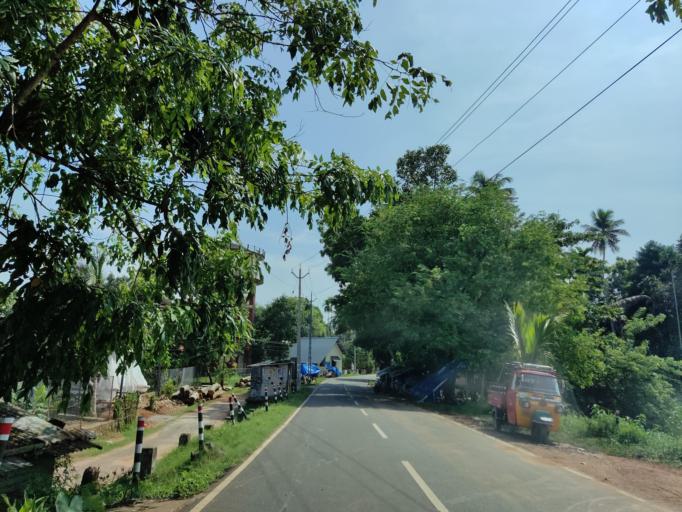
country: IN
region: Kerala
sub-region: Alappuzha
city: Mavelikara
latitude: 9.3245
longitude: 76.4633
